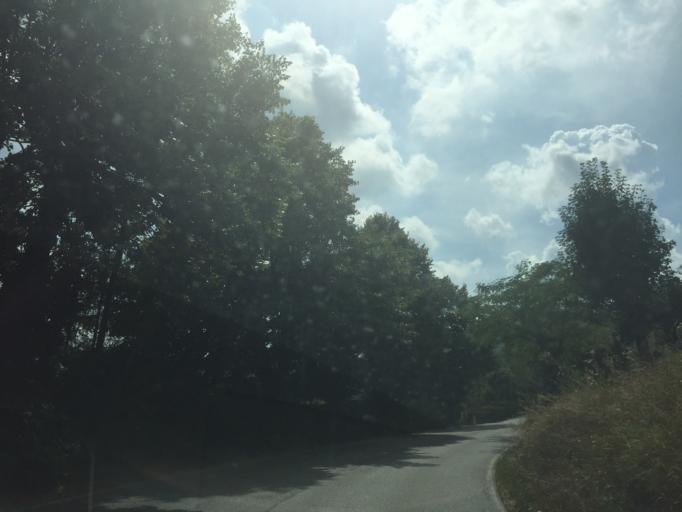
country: IT
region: Tuscany
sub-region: Provincia di Pistoia
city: Campo Tizzoro
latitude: 44.0434
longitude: 10.8426
